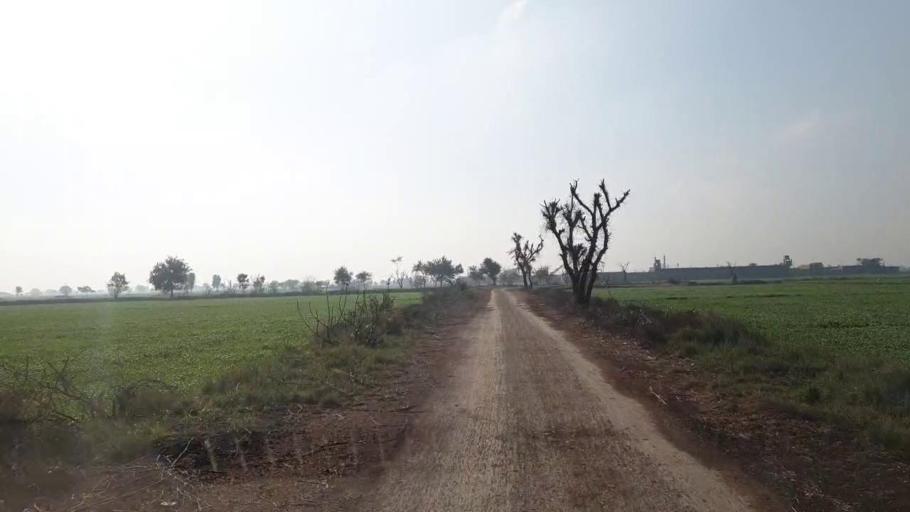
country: PK
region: Sindh
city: Shahdadpur
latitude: 25.9947
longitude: 68.6246
